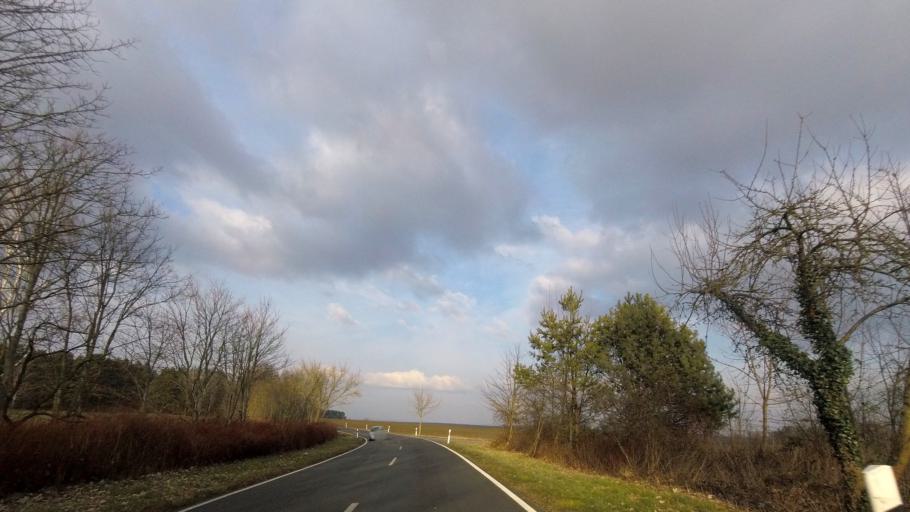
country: DE
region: Brandenburg
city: Belzig
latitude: 52.1208
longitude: 12.5829
